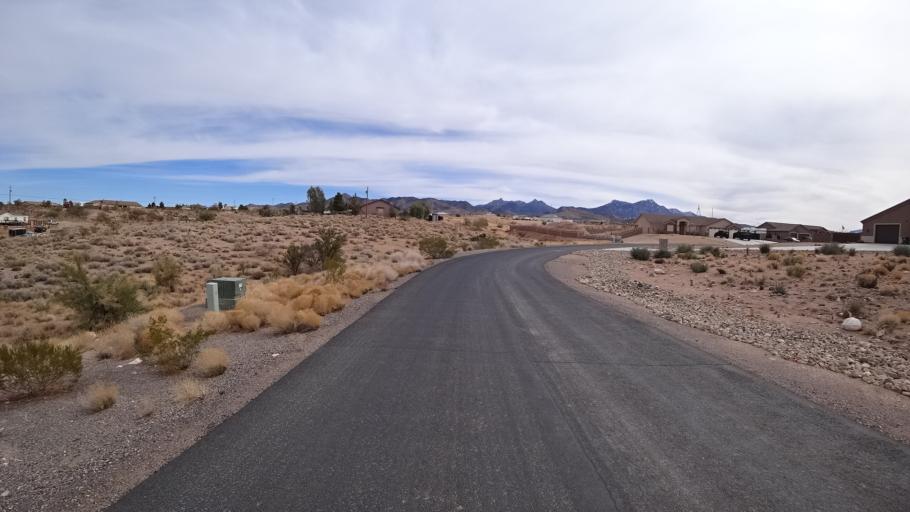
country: US
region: Arizona
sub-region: Mohave County
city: Kingman
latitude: 35.1771
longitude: -113.9950
